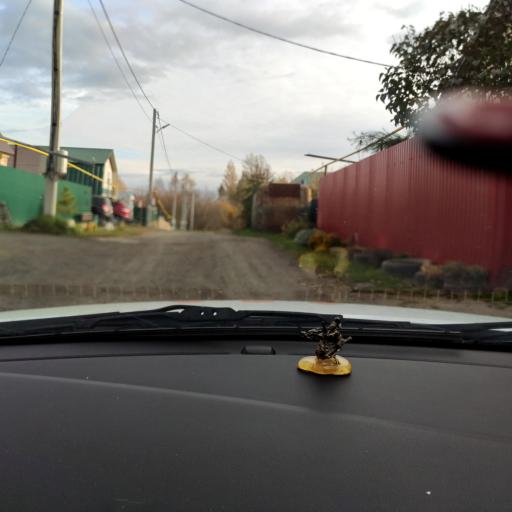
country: RU
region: Tatarstan
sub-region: Gorod Kazan'
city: Kazan
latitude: 55.7372
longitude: 49.0958
